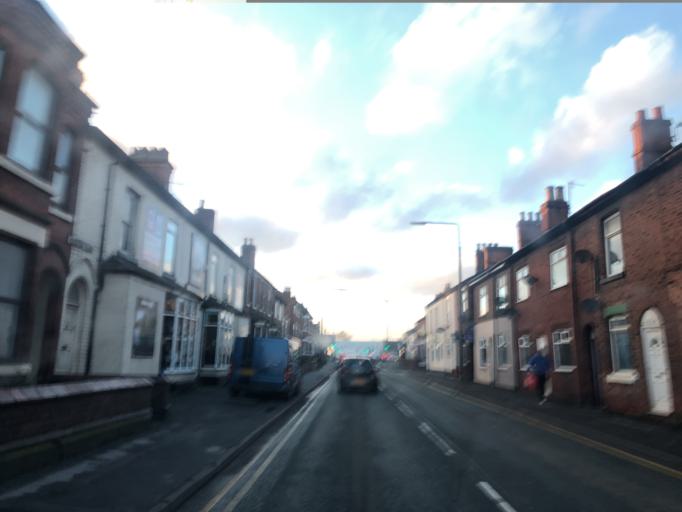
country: GB
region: England
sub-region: Cheshire West and Chester
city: Marston
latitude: 53.2615
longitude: -2.4984
